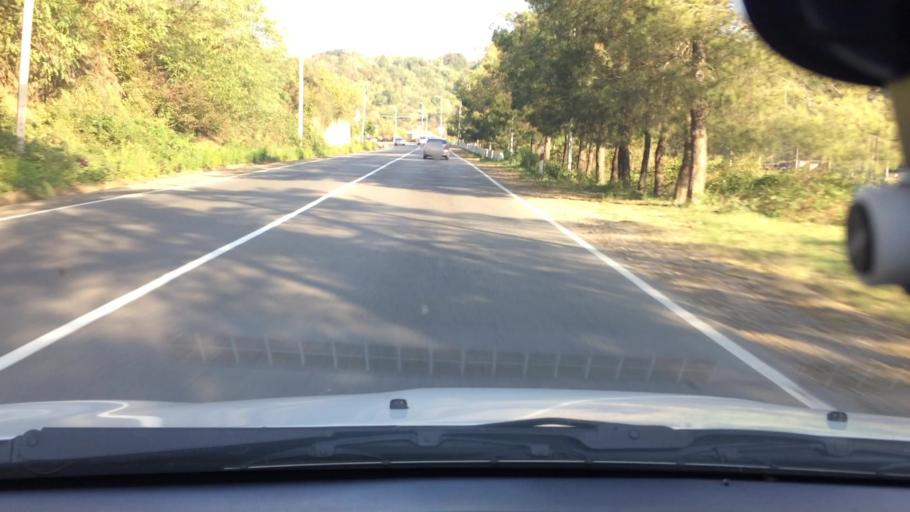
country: GE
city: Shorapani
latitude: 42.0981
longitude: 43.0749
